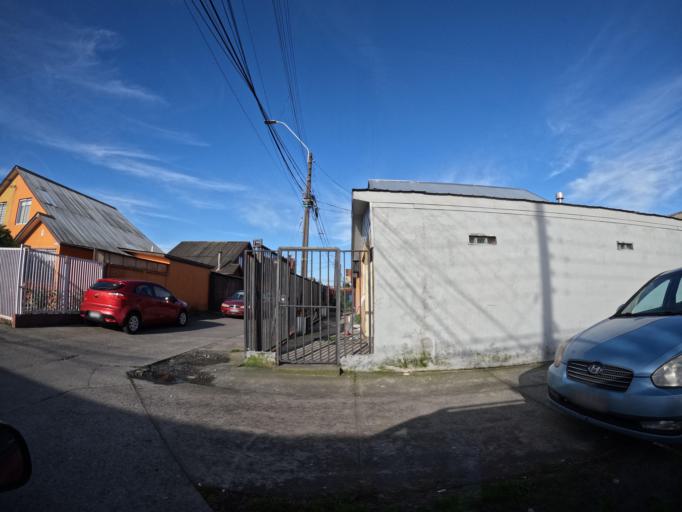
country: CL
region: Biobio
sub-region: Provincia de Concepcion
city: Talcahuano
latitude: -36.7465
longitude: -73.0857
